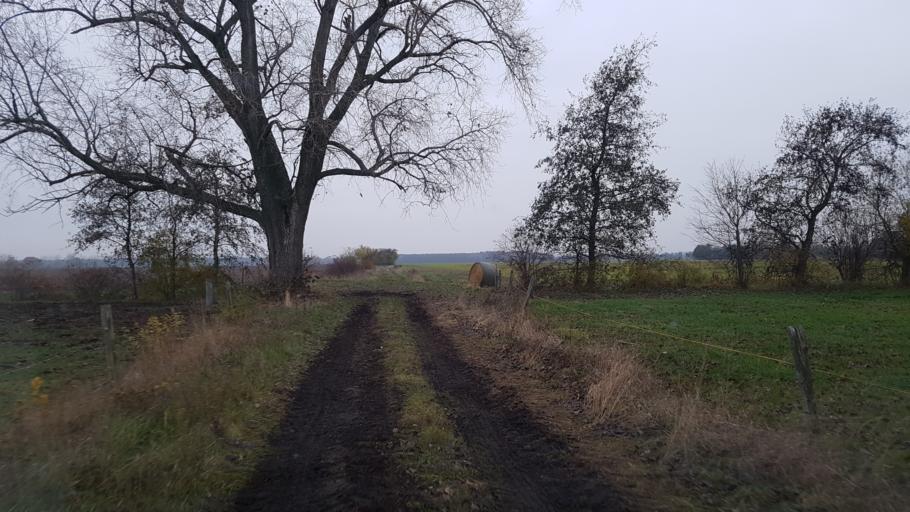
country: DE
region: Brandenburg
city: Schilda
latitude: 51.6201
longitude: 13.3495
